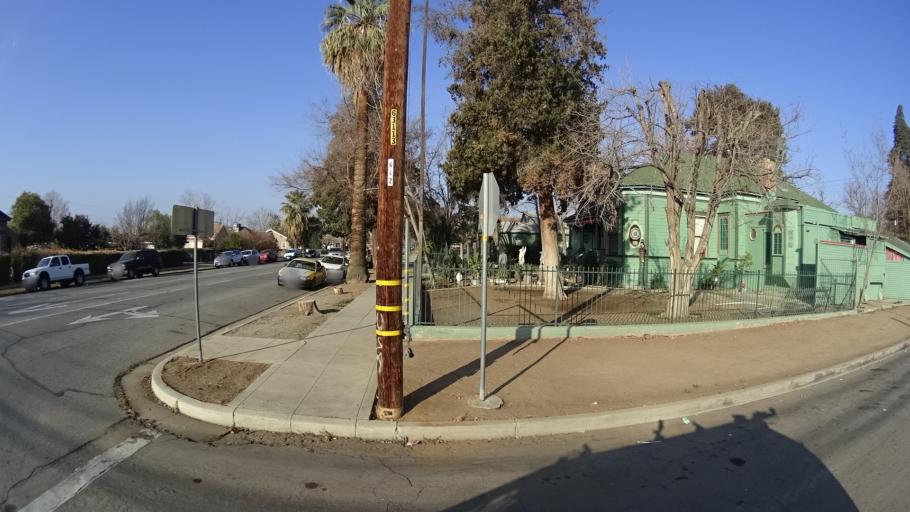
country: US
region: California
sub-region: Kern County
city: Bakersfield
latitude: 35.3815
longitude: -118.9929
